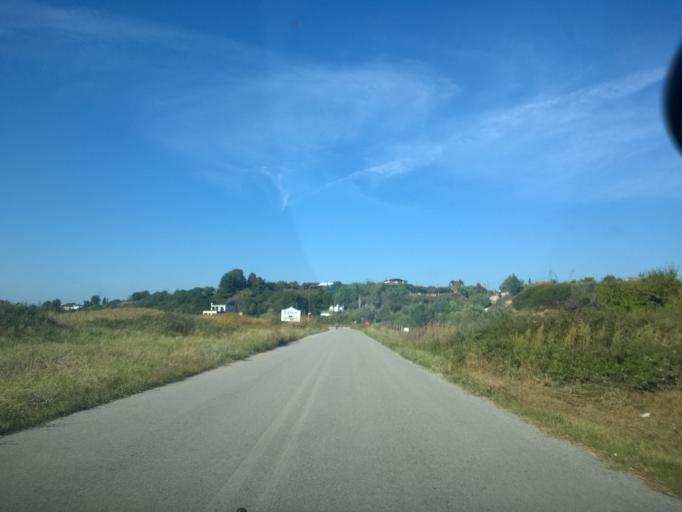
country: GR
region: Central Macedonia
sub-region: Nomos Chalkidikis
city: Nea Kallikrateia
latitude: 40.3310
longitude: 23.0241
